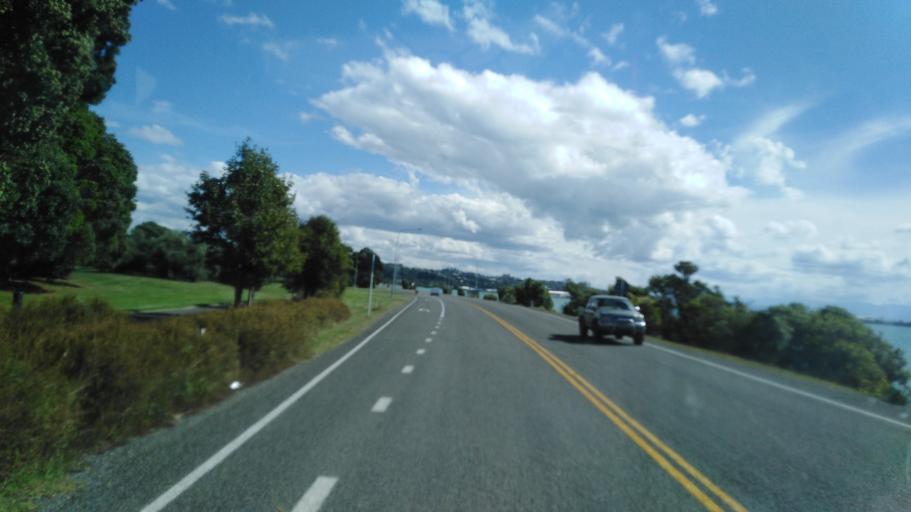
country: NZ
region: Nelson
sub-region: Nelson City
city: Nelson
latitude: -41.2551
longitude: 173.3007
